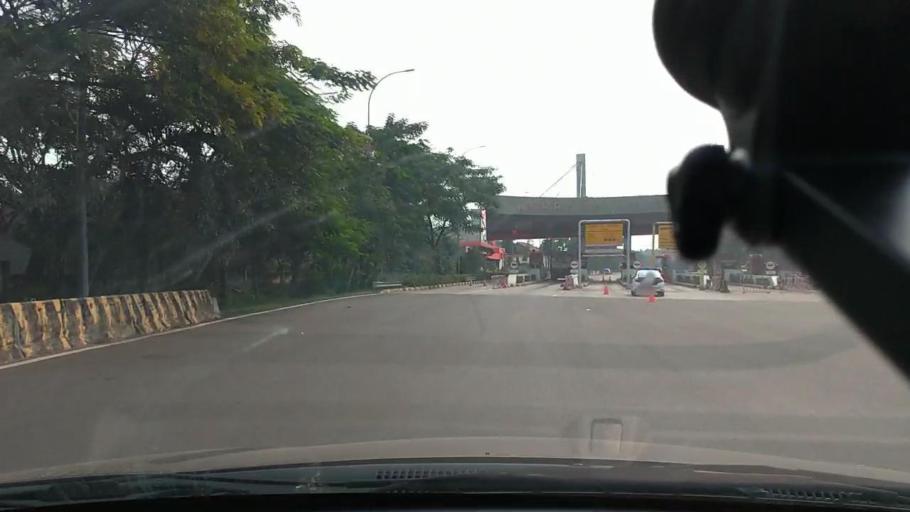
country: ID
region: Banten
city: Serang
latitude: -6.0910
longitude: 106.1369
